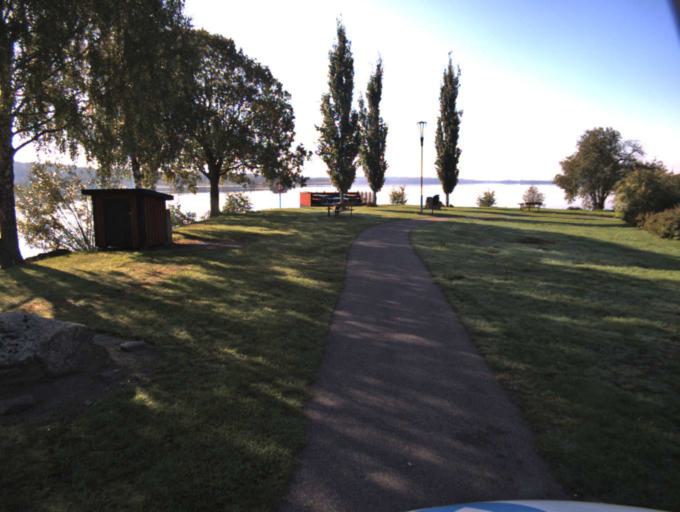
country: SE
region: Vaestra Goetaland
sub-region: Ulricehamns Kommun
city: Ulricehamn
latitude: 57.6790
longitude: 13.3782
